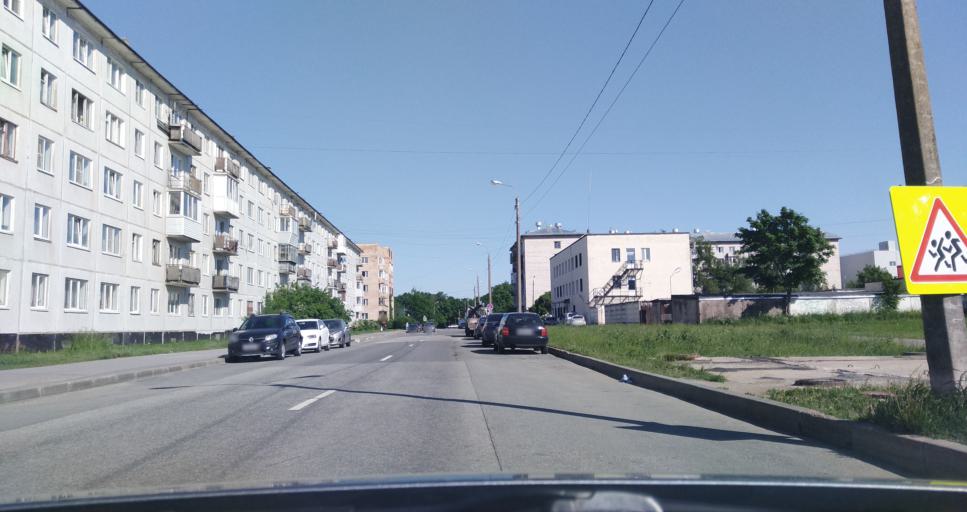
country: RU
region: St.-Petersburg
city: Krasnoye Selo
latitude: 59.7430
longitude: 30.0883
